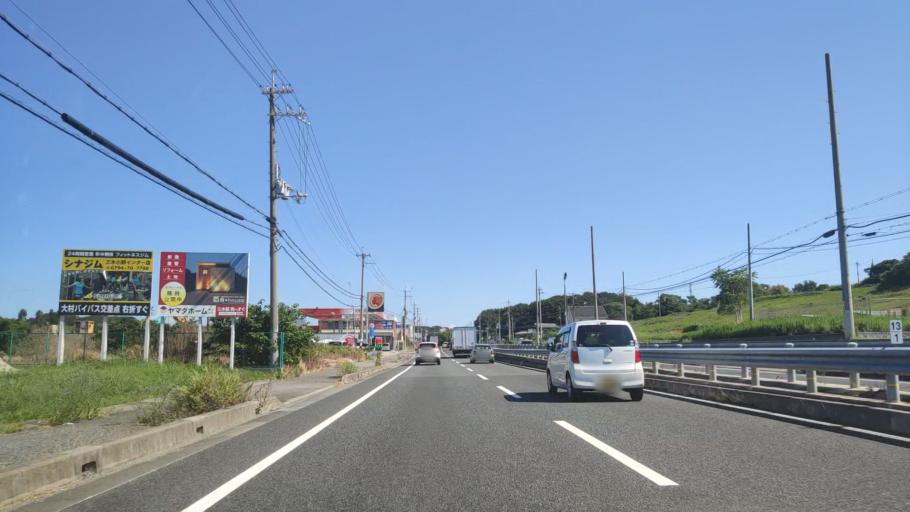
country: JP
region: Hyogo
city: Miki
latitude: 34.7670
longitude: 134.9812
